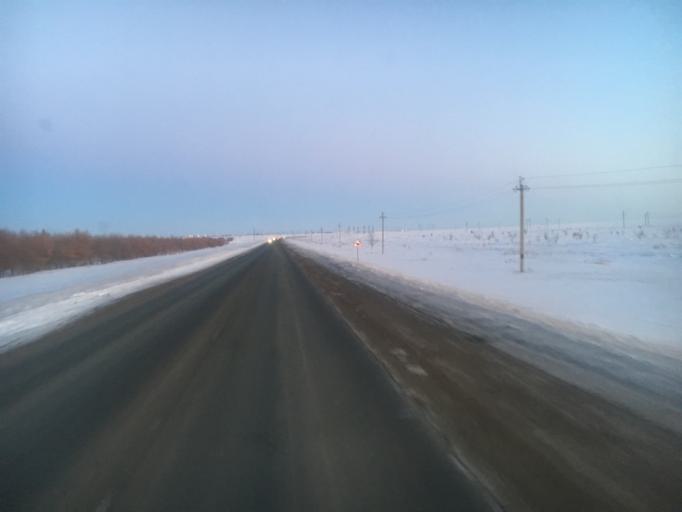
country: KZ
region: Batys Qazaqstan
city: Krugloozernoe
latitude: 51.1490
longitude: 51.3133
